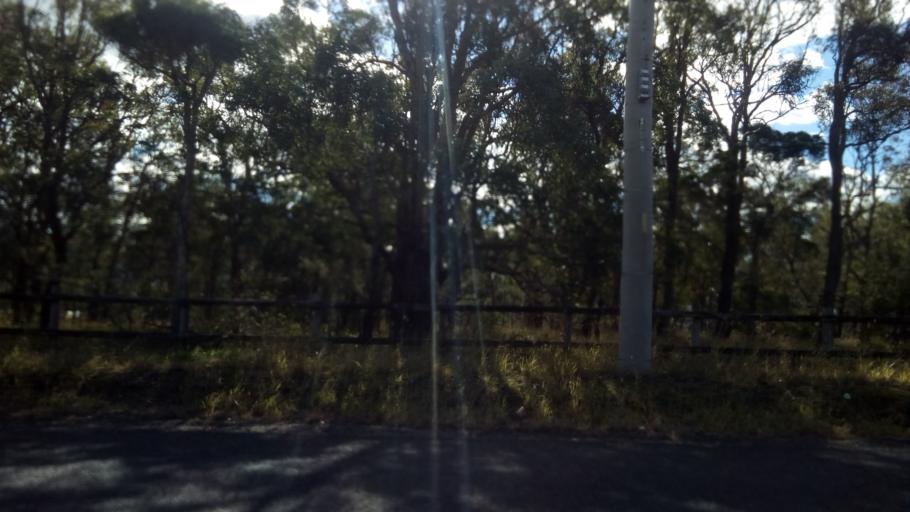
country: AU
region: New South Wales
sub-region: Shellharbour
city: Albion Park Rail
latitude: -34.5379
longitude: 150.7794
